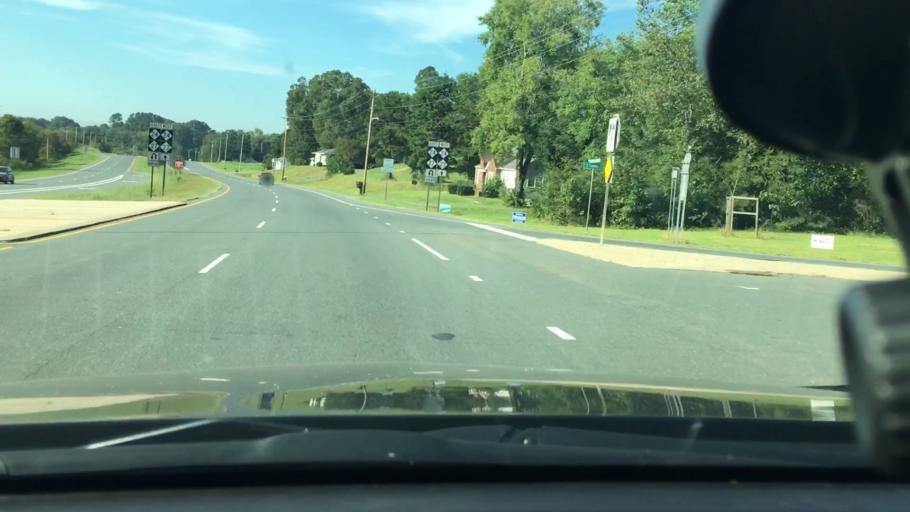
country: US
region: North Carolina
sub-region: Stanly County
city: Albemarle
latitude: 35.3325
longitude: -80.2341
